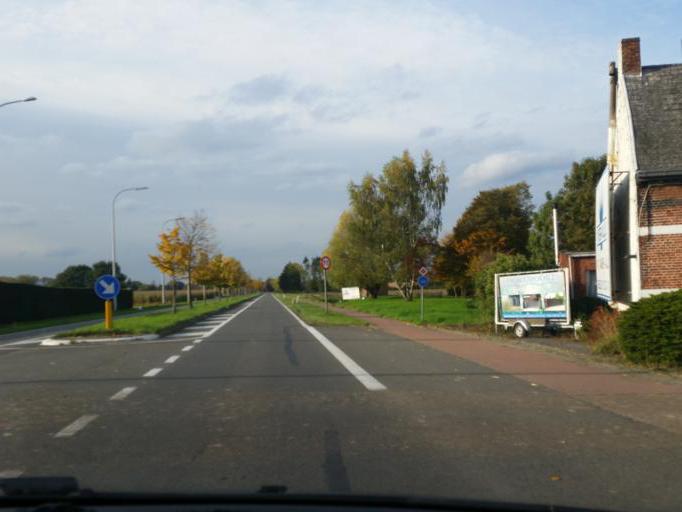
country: BE
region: Flanders
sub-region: Provincie Antwerpen
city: Lier
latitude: 51.1028
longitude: 4.6088
